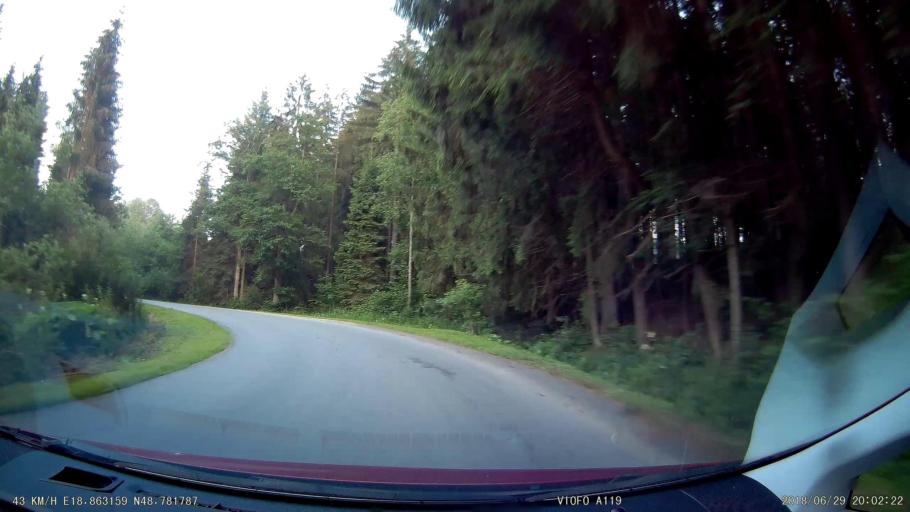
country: SK
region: Banskobystricky
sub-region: Okres Ziar nad Hronom
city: Kremnica
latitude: 48.7819
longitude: 18.8628
